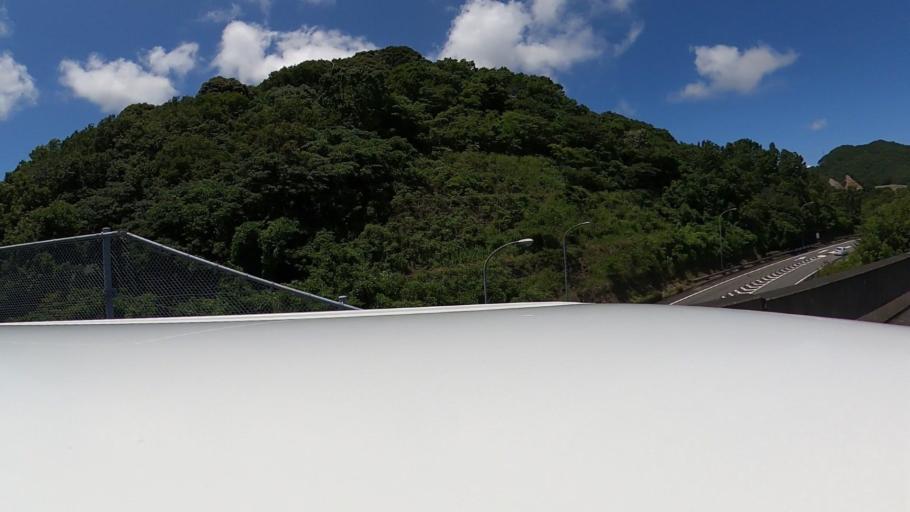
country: JP
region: Miyazaki
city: Nobeoka
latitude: 32.5000
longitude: 131.6613
